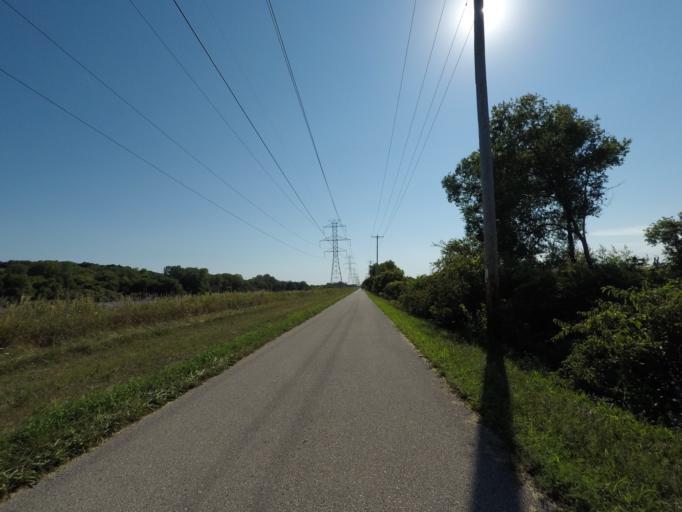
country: US
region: Wisconsin
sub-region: Waukesha County
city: New Berlin
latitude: 43.0098
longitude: -88.1626
